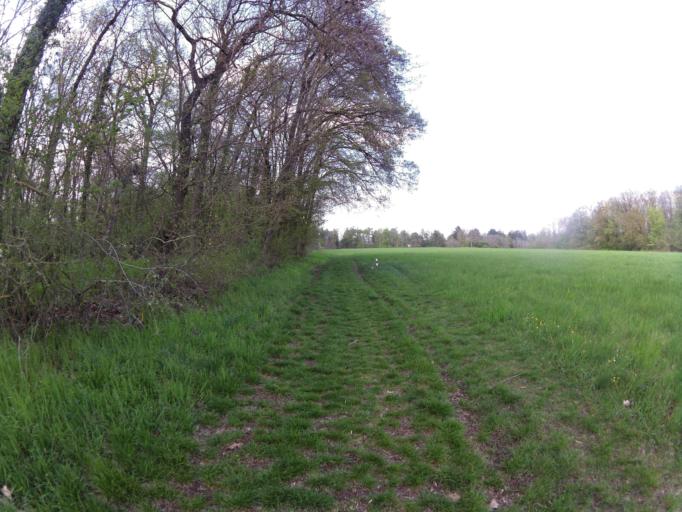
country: DE
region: Bavaria
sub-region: Regierungsbezirk Unterfranken
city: Winterhausen
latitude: 49.6970
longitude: 10.0060
